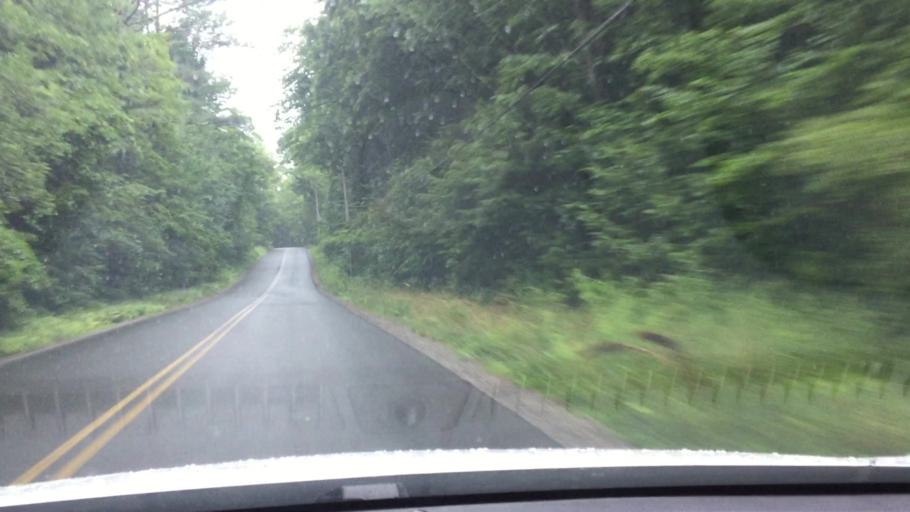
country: US
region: Massachusetts
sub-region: Berkshire County
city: Becket
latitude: 42.2728
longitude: -73.0192
